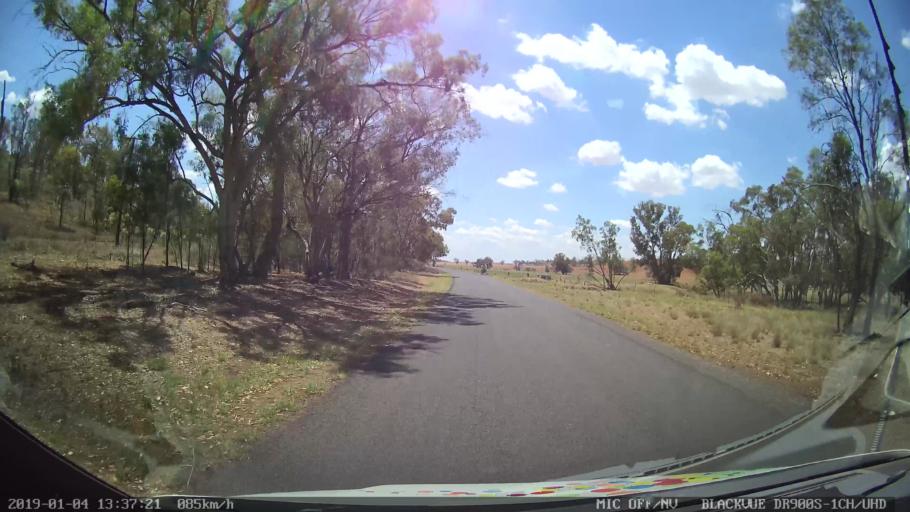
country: AU
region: New South Wales
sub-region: Dubbo Municipality
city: Dubbo
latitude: -32.5511
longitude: 148.5430
